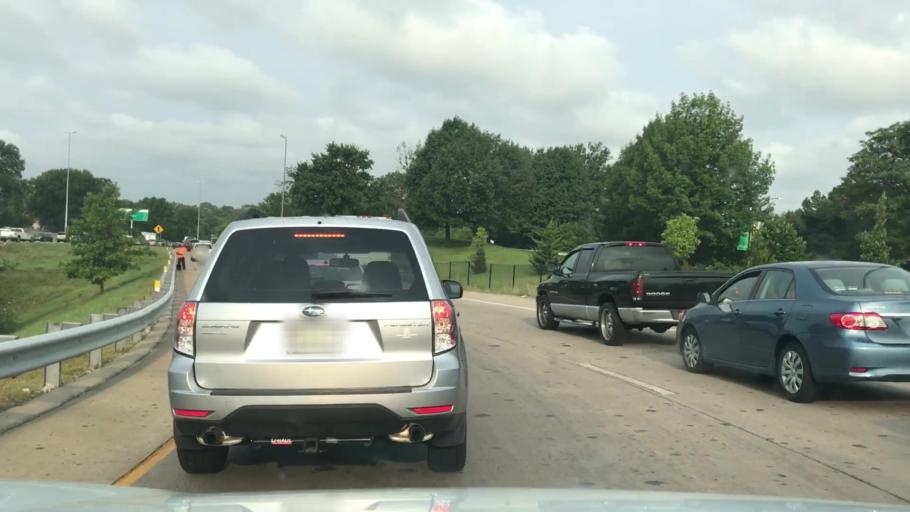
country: US
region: Missouri
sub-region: Saint Louis County
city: University City
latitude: 38.6327
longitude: -90.2872
